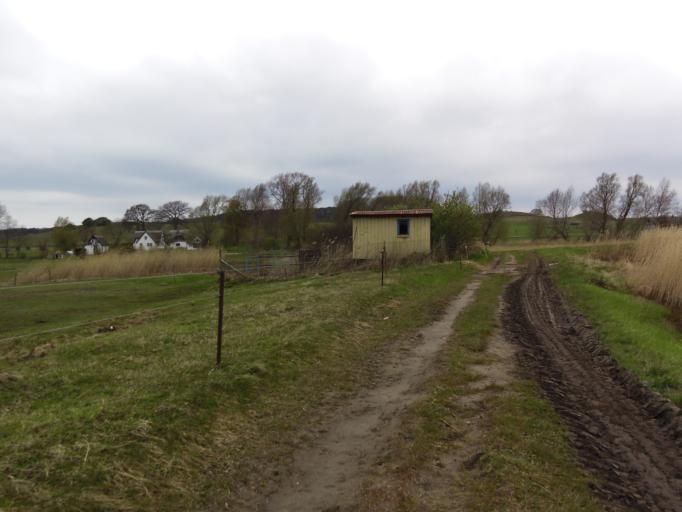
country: DE
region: Mecklenburg-Vorpommern
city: Hiddensee
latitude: 54.5891
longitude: 13.1264
